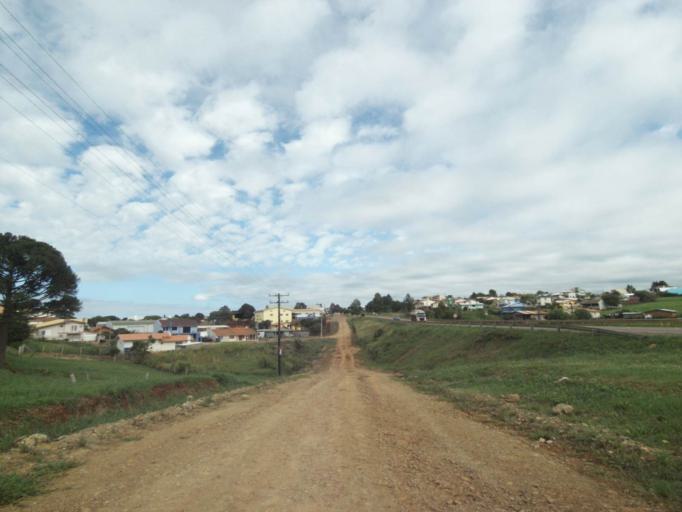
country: BR
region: Rio Grande do Sul
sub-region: Lagoa Vermelha
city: Lagoa Vermelha
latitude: -28.2090
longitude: -51.5134
